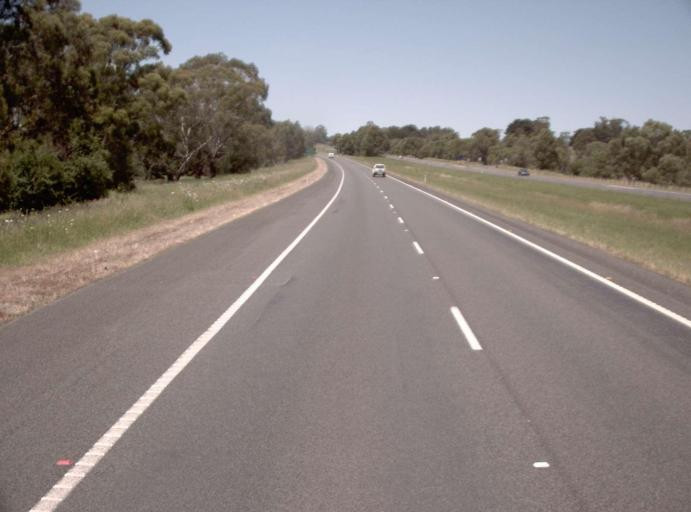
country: AU
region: Victoria
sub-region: Baw Baw
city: Warragul
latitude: -38.1272
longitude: 145.8739
